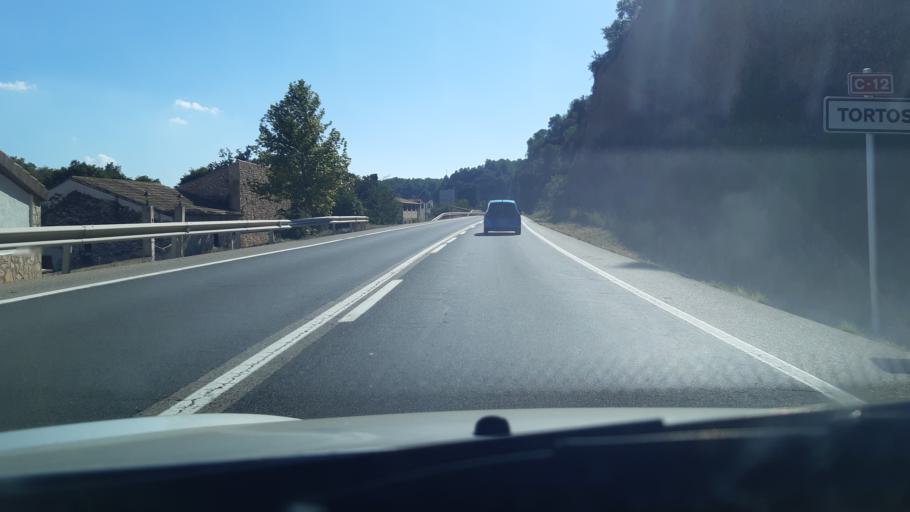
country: ES
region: Catalonia
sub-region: Provincia de Tarragona
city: Tivenys
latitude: 40.8750
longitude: 0.5009
